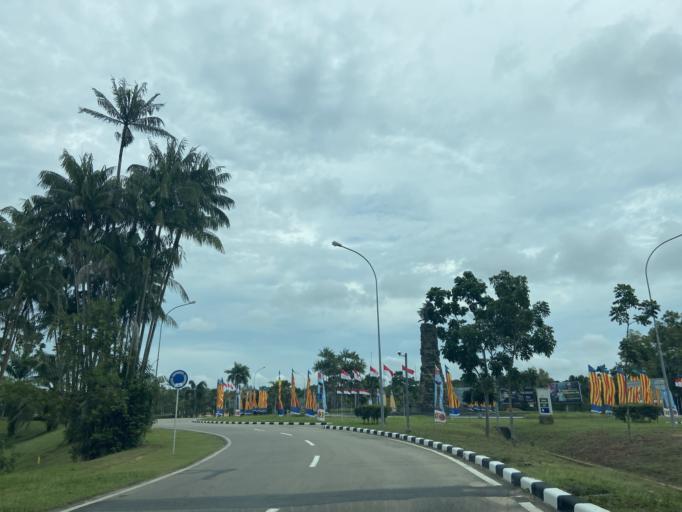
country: SG
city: Singapore
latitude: 1.1238
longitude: 104.1130
